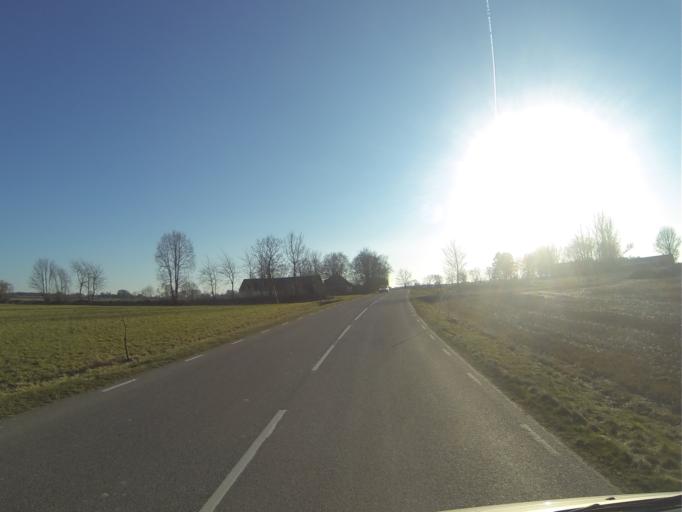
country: SE
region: Skane
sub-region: Hoors Kommun
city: Loberod
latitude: 55.7859
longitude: 13.5304
